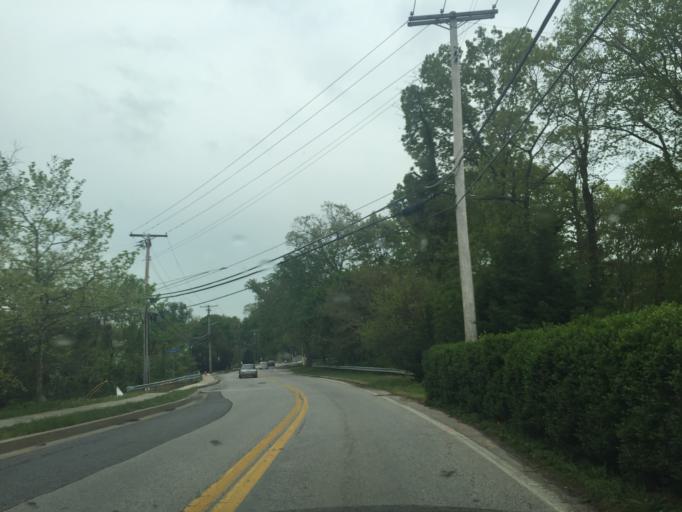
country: US
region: Maryland
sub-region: Baltimore County
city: Catonsville
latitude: 39.2646
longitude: -76.7297
